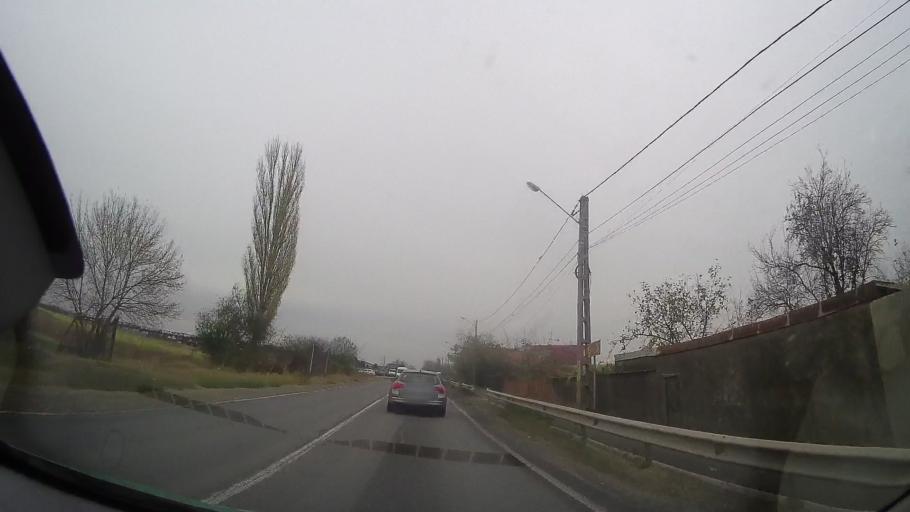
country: RO
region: Prahova
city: Ploiesti
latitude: 44.9633
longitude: 26.0356
